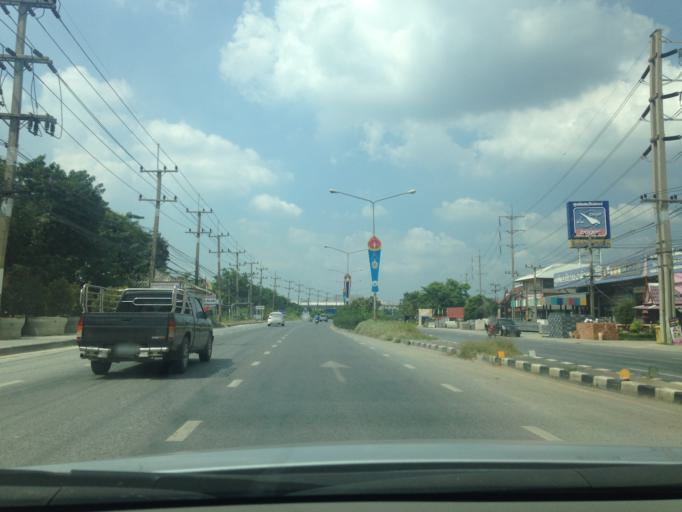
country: TH
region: Pathum Thani
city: Sam Khok
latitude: 14.0704
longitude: 100.5223
